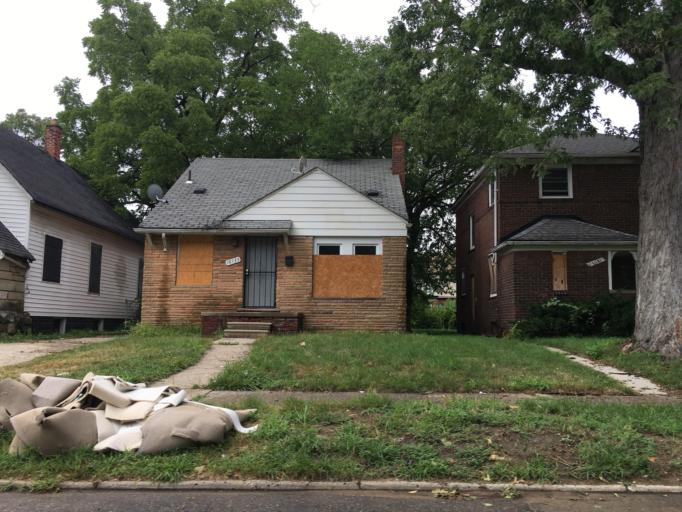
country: US
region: Michigan
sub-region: Oakland County
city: Ferndale
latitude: 42.4104
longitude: -83.1546
